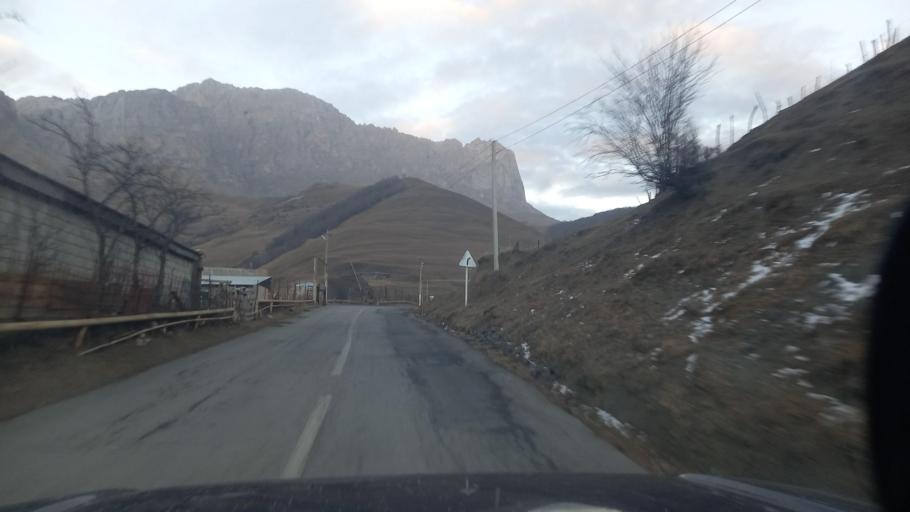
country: RU
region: Ingushetiya
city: Dzhayrakh
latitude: 42.8113
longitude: 44.7998
